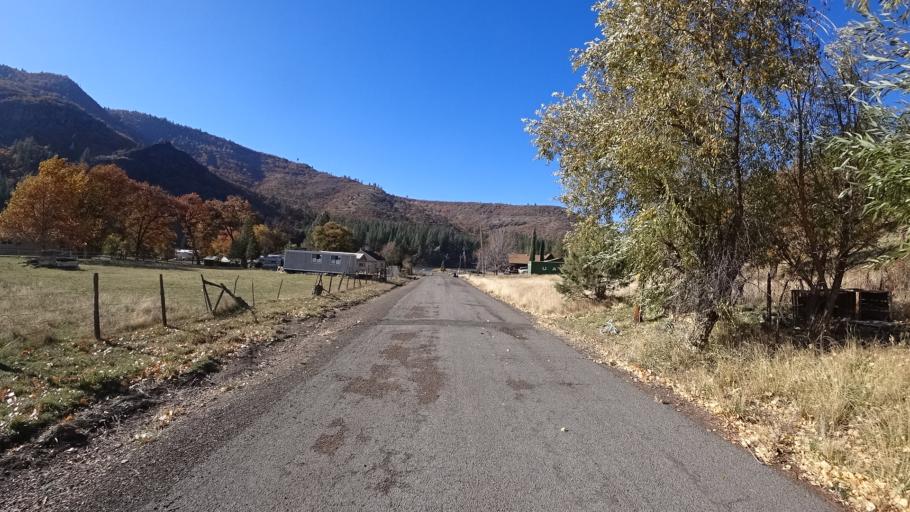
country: US
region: California
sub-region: Siskiyou County
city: Montague
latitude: 41.9668
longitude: -122.2633
